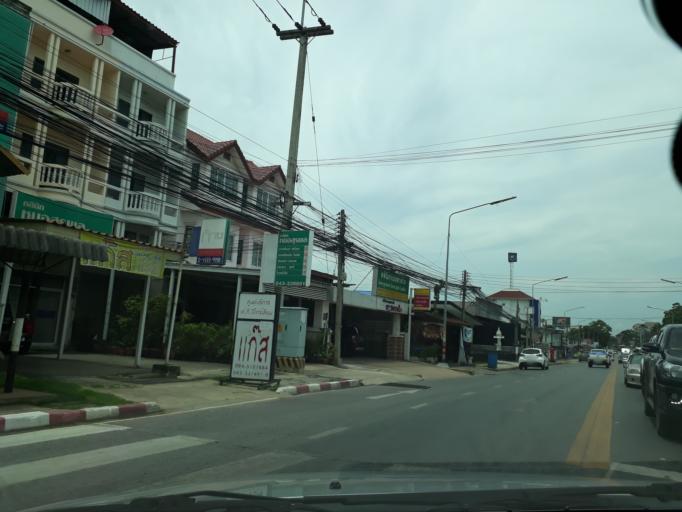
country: TH
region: Khon Kaen
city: Khon Kaen
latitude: 16.4352
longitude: 102.8541
